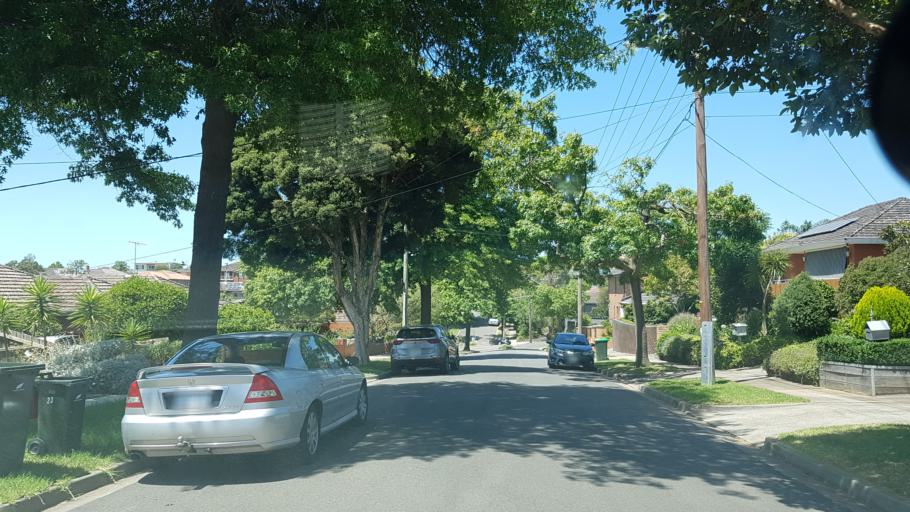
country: AU
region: Victoria
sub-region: Manningham
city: Bulleen
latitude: -37.7597
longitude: 145.0998
